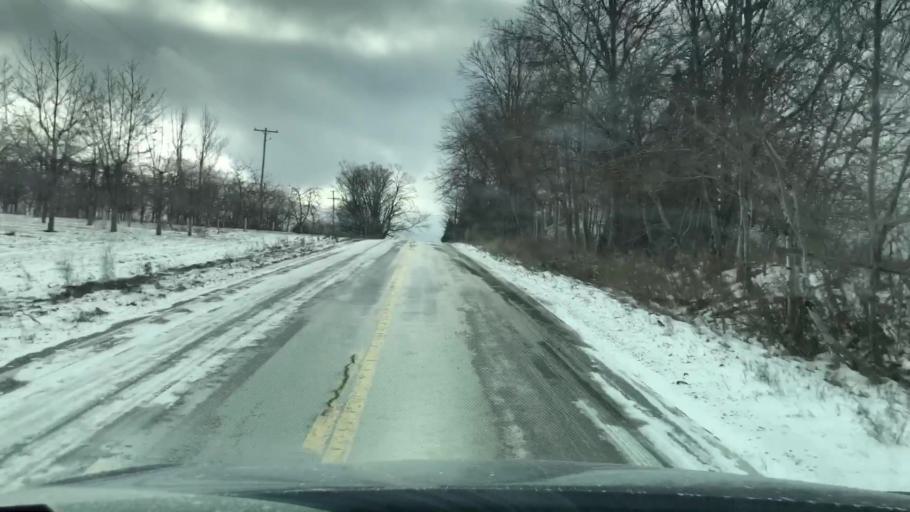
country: US
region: Michigan
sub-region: Antrim County
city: Elk Rapids
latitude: 44.9369
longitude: -85.5156
